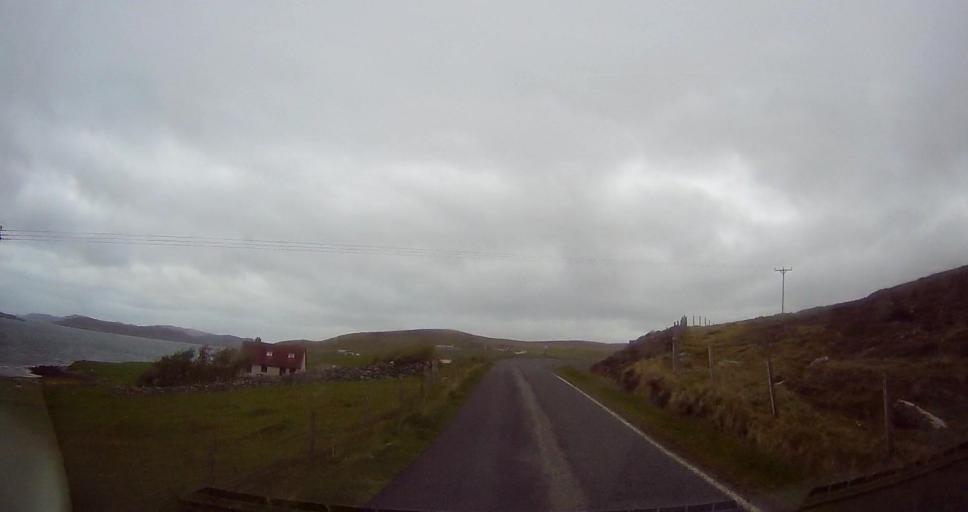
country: GB
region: Scotland
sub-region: Shetland Islands
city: Lerwick
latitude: 60.2981
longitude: -1.3602
